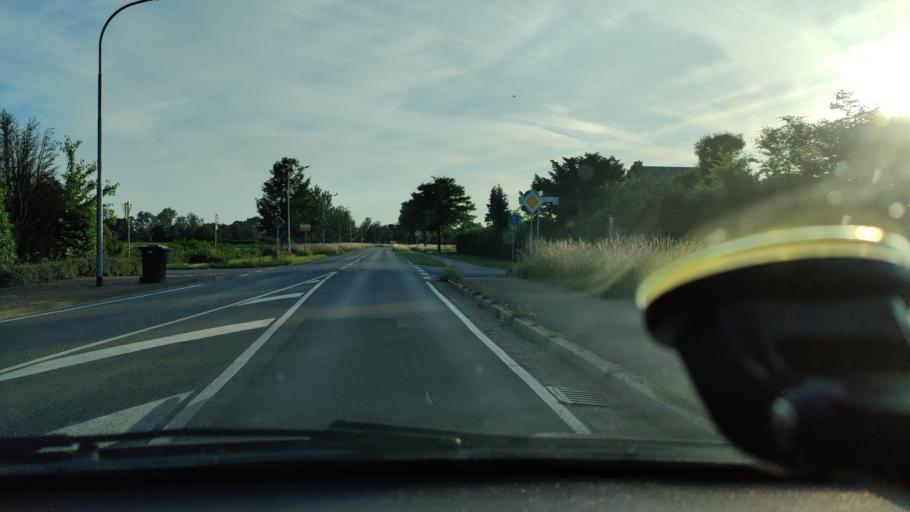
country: DE
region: North Rhine-Westphalia
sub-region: Regierungsbezirk Dusseldorf
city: Rheurdt
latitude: 51.4915
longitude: 6.4476
